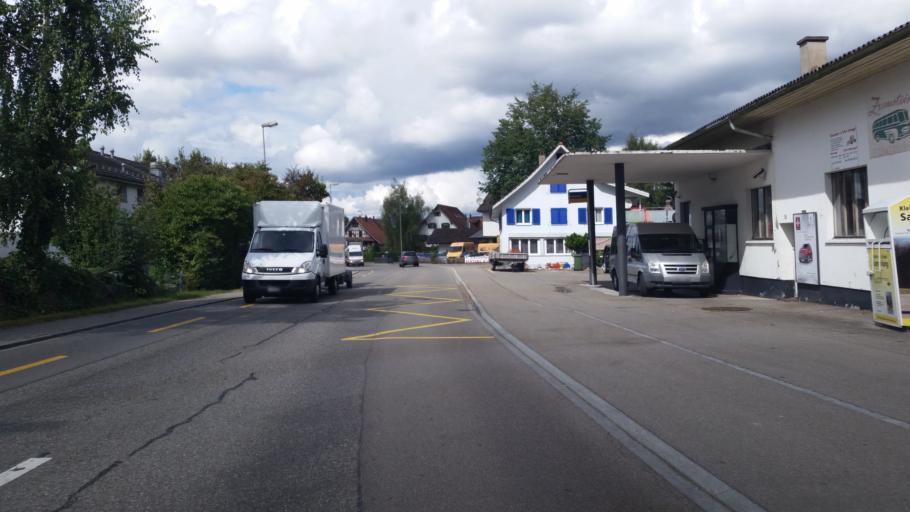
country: CH
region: Zurich
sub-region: Bezirk Affoltern
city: Ottenbach
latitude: 47.2775
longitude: 8.4077
